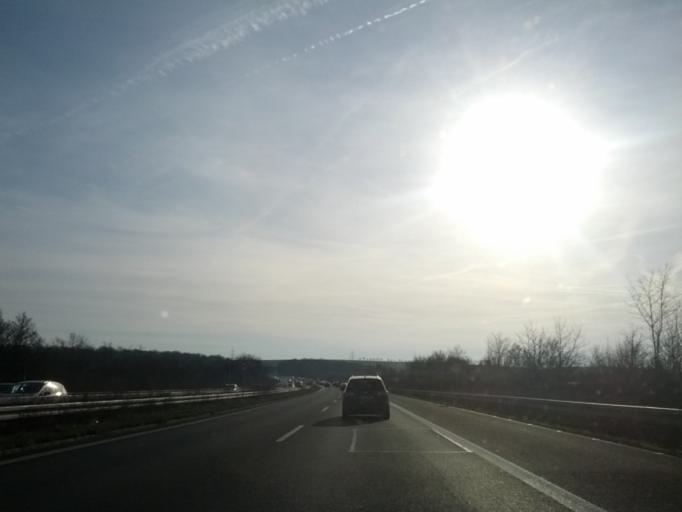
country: DE
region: Bavaria
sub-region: Regierungsbezirk Unterfranken
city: Rottendorf
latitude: 49.8081
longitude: 10.0443
